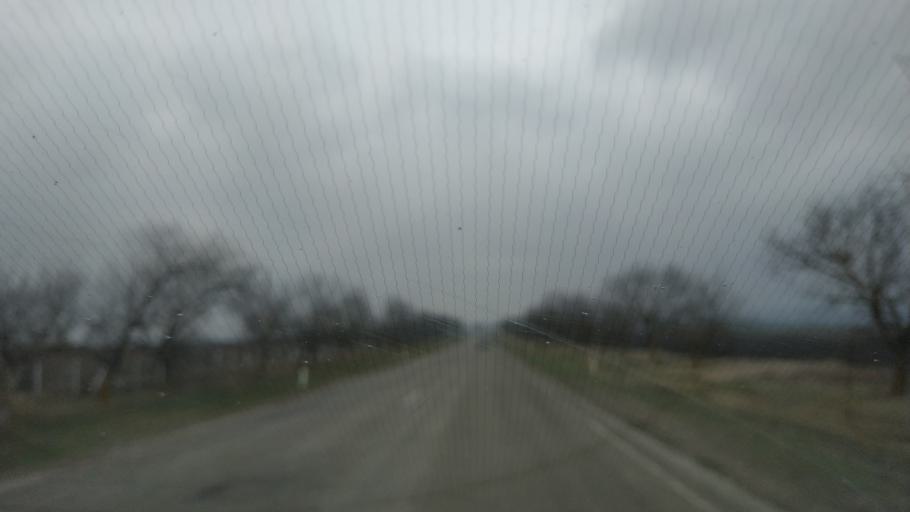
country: MD
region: Gagauzia
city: Comrat
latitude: 46.2641
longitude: 28.7423
